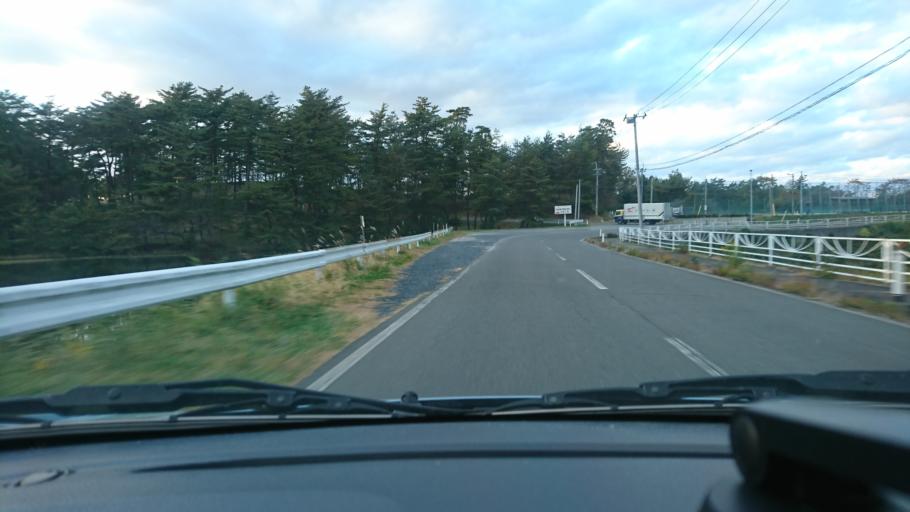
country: JP
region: Iwate
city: Ichinoseki
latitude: 38.8040
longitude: 141.1923
